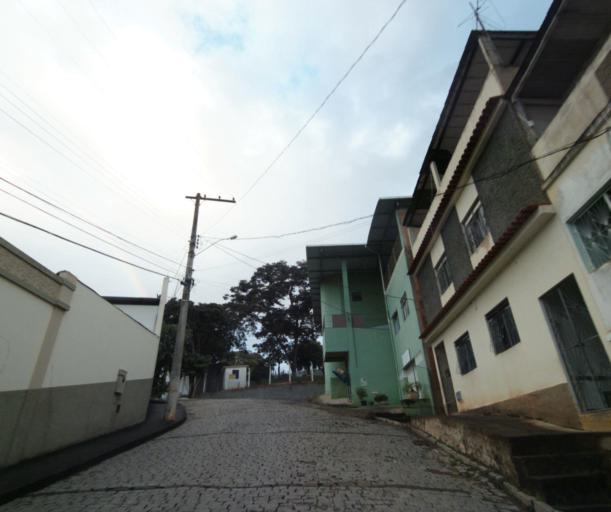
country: BR
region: Espirito Santo
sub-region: Muniz Freire
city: Muniz Freire
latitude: -20.4654
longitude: -41.4126
